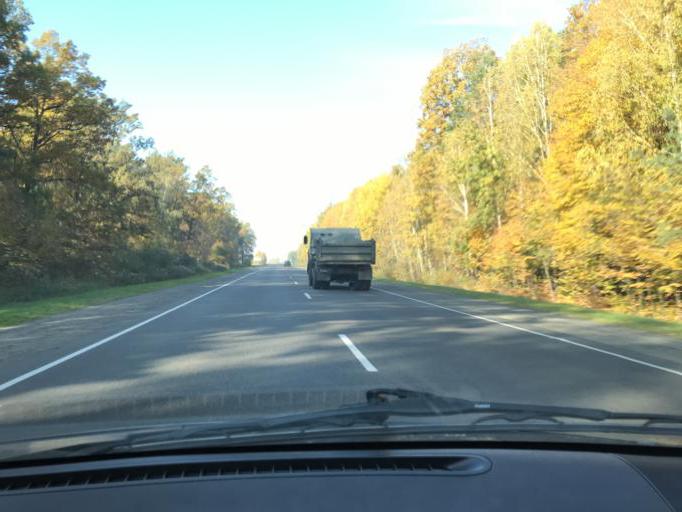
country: BY
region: Brest
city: Horad Luninyets
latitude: 52.3088
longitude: 26.6793
